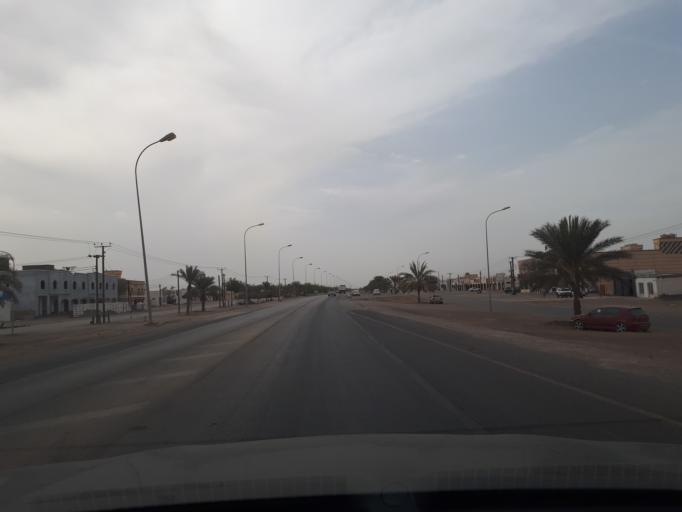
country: OM
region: Ash Sharqiyah
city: Badiyah
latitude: 22.4548
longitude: 58.8062
